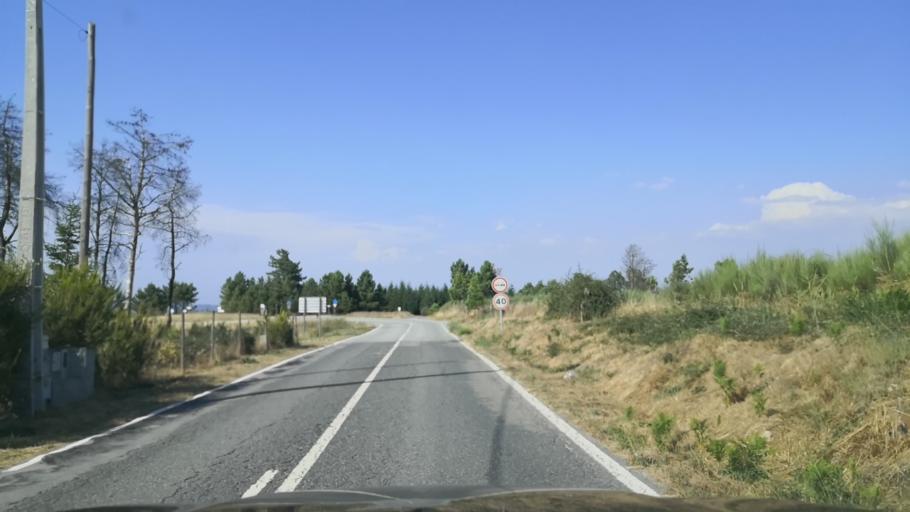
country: PT
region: Vila Real
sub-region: Murca
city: Murca
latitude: 41.3142
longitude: -7.4696
